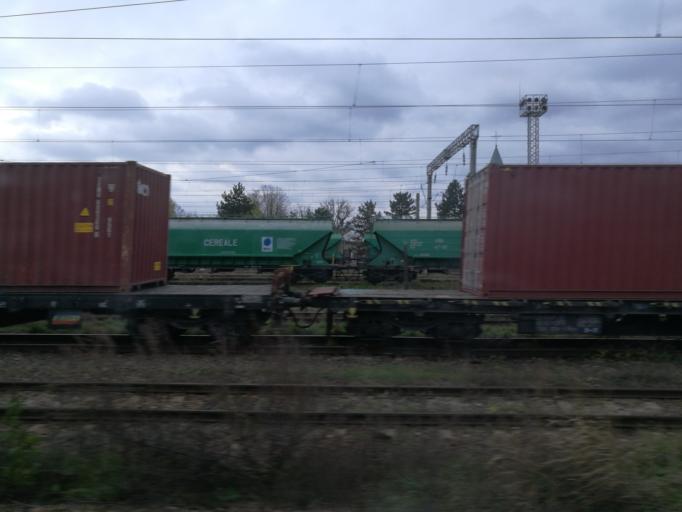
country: RO
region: Bacau
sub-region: Municipiul Bacau
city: Bacau
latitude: 46.5608
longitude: 26.8995
